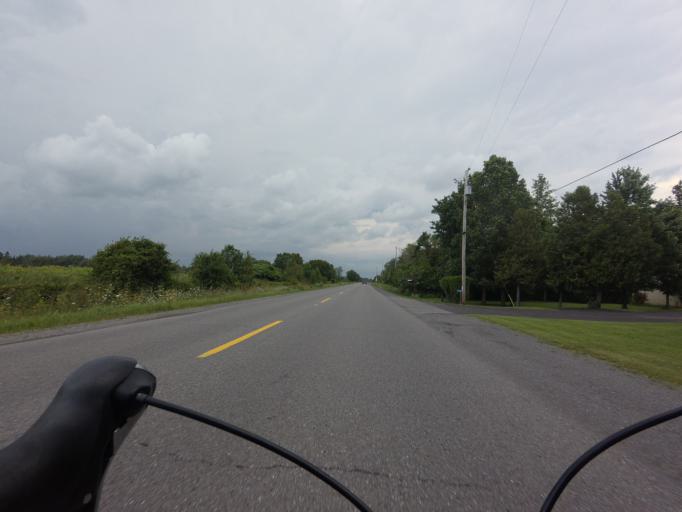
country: CA
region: Ontario
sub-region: Lanark County
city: Smiths Falls
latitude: 44.8304
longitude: -75.8160
